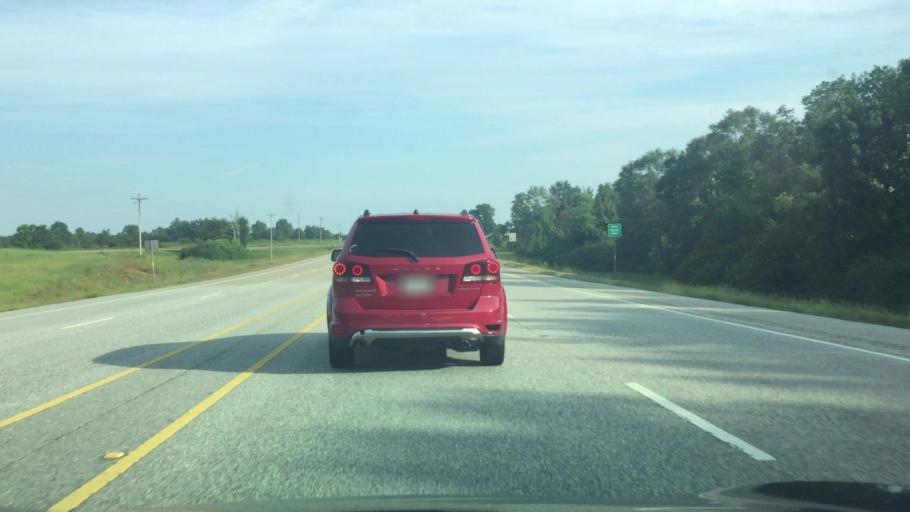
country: US
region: Alabama
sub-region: Butler County
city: Georgiana
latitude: 31.5238
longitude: -86.7160
